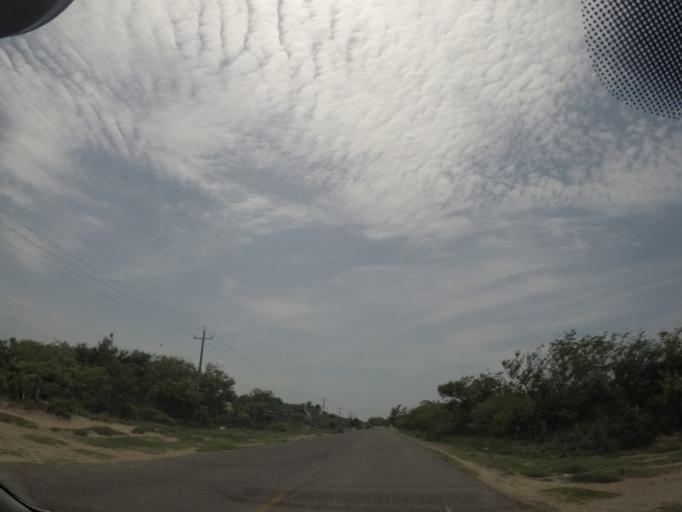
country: MX
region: Oaxaca
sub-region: San Mateo del Mar
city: Colonia Juarez
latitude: 16.2091
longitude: -95.0401
